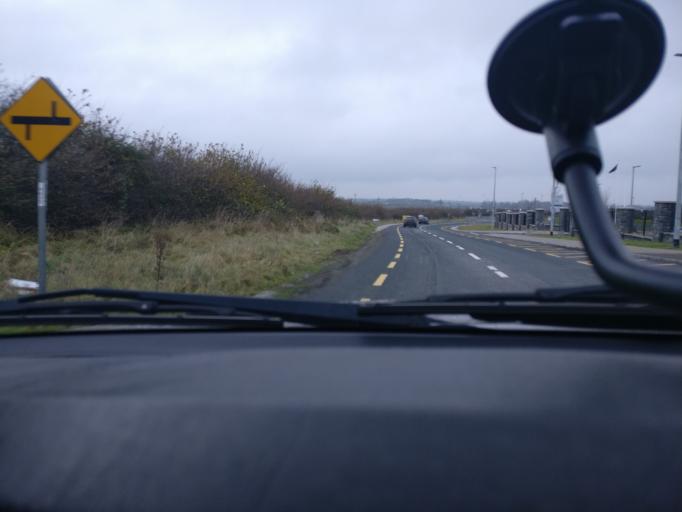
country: IE
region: Connaught
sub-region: County Galway
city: Loughrea
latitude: 53.2045
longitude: -8.5855
